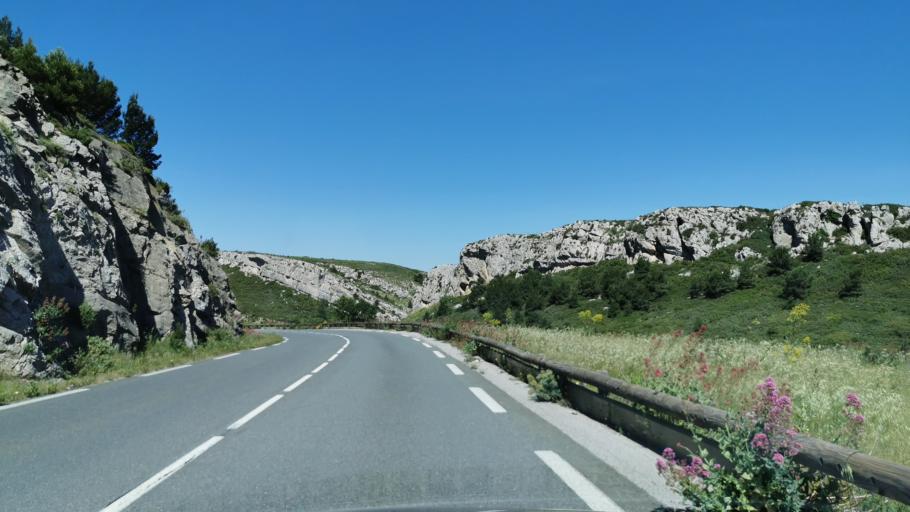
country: FR
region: Languedoc-Roussillon
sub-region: Departement de l'Aude
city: Armissan
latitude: 43.1772
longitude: 3.0988
